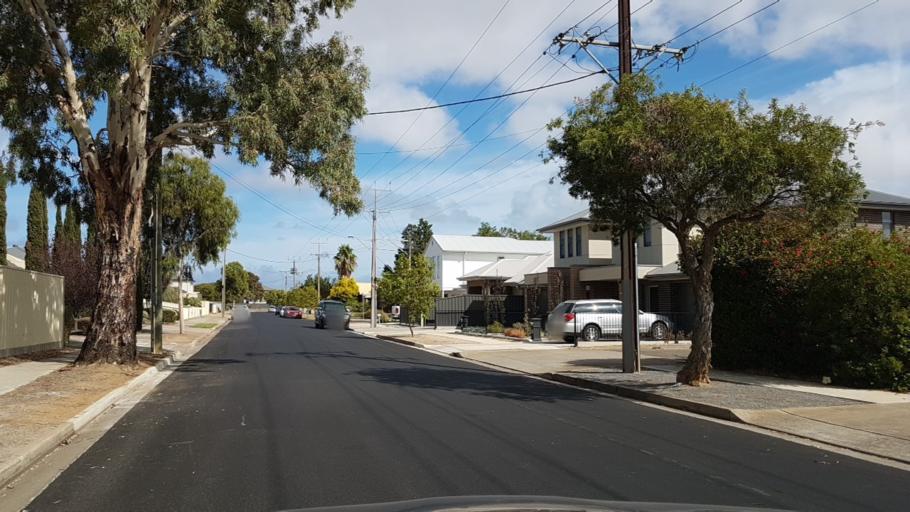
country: AU
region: South Australia
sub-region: Marion
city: Plympton Park
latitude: -34.9828
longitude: 138.5497
